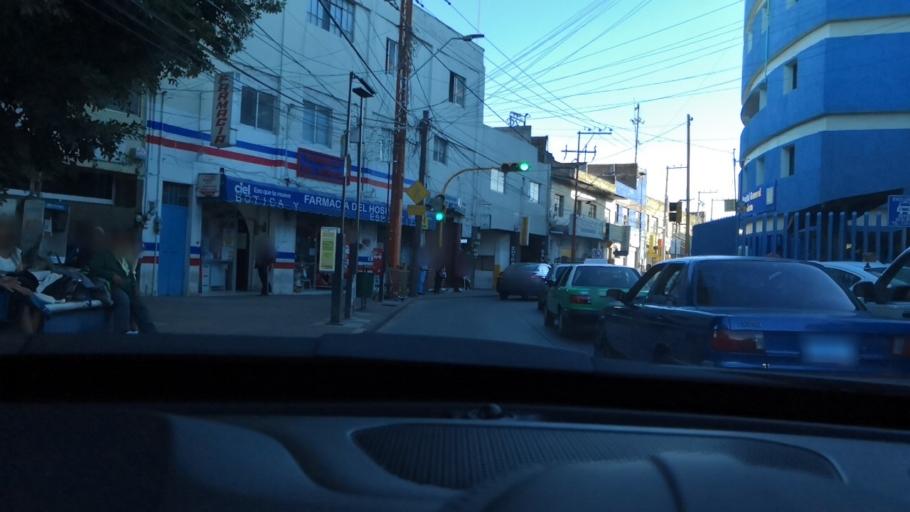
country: MX
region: Guanajuato
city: Leon
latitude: 21.1330
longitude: -101.6797
